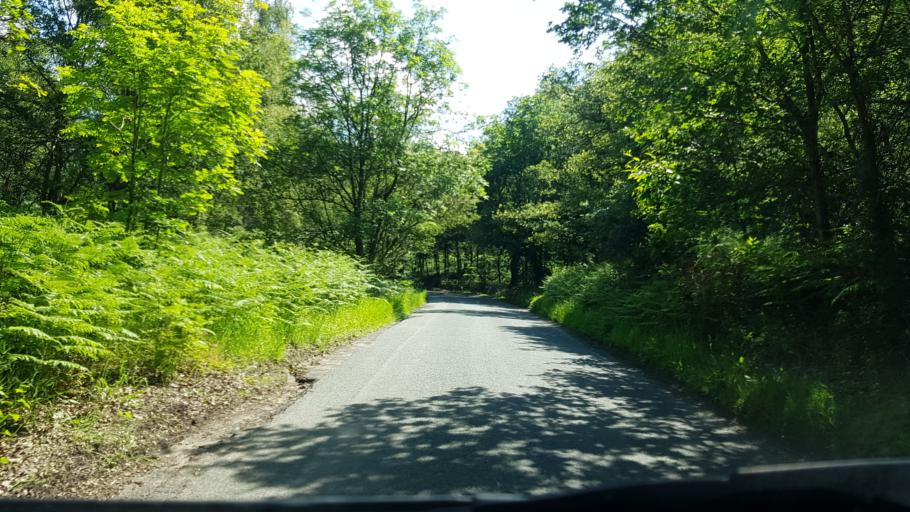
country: GB
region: England
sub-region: Worcestershire
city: Kidderminster
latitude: 52.4448
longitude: -2.2552
